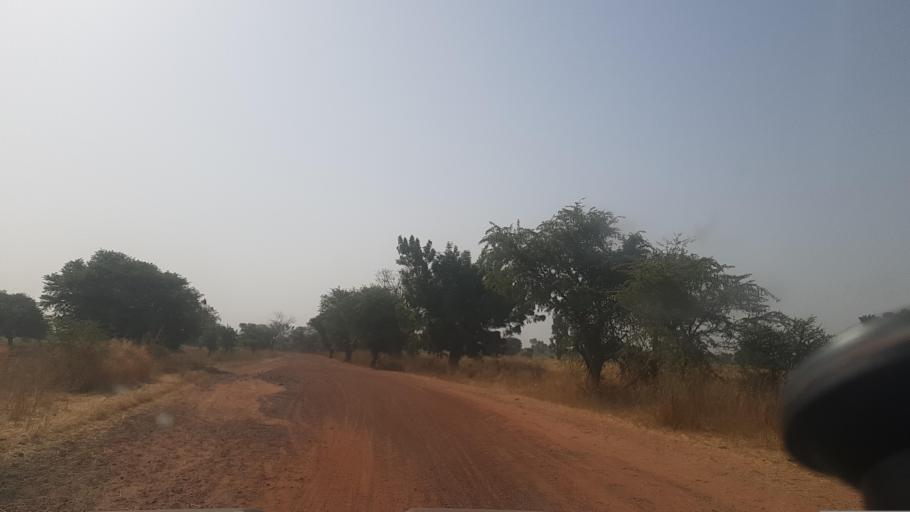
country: ML
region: Segou
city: Baroueli
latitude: 13.1468
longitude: -6.5159
